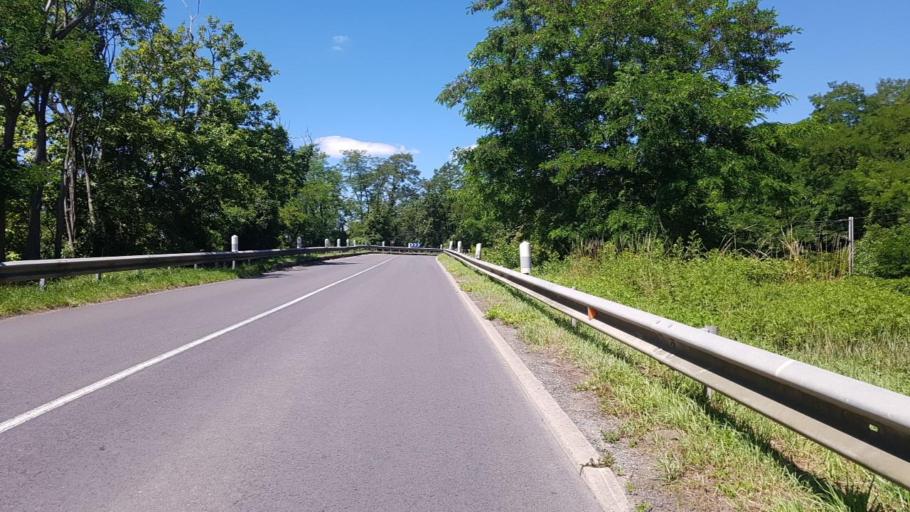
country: FR
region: Ile-de-France
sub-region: Departement de Seine-et-Marne
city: Sammeron
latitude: 48.9534
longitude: 3.0948
